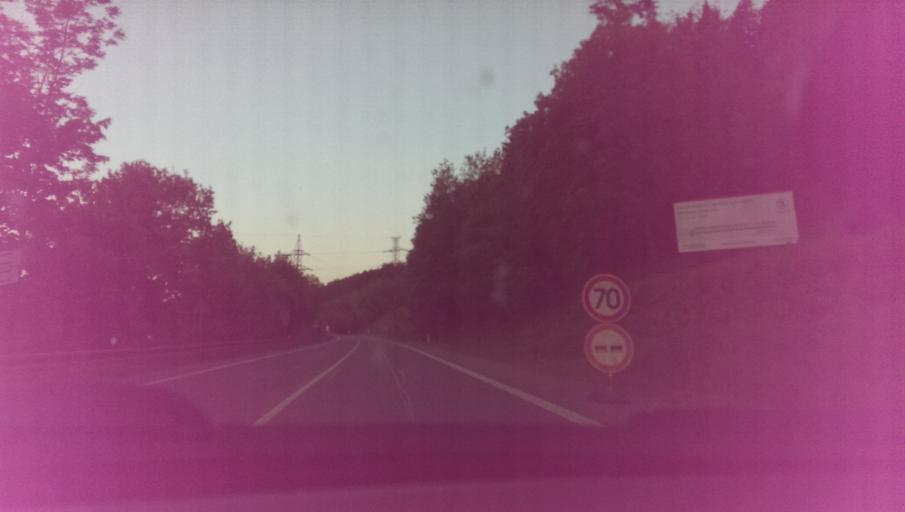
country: CZ
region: Zlin
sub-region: Okres Vsetin
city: Vsetin
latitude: 49.3401
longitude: 17.9757
